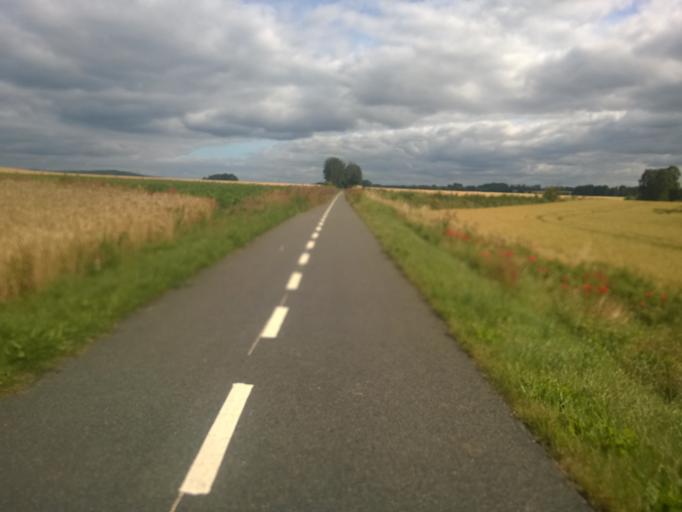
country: SE
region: Skane
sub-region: Kristianstads Kommun
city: Kristianstad
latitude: 56.0616
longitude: 14.1844
